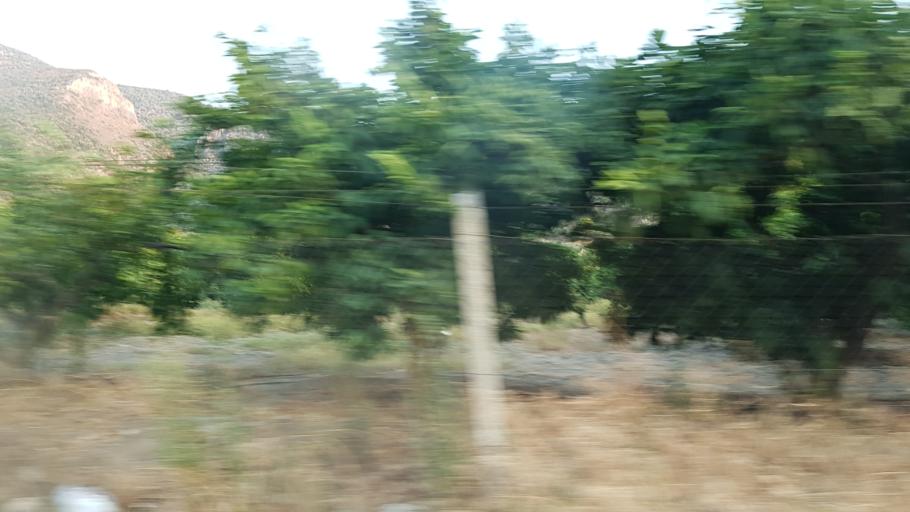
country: TR
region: Izmir
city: Selcuk
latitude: 37.9601
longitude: 27.3932
